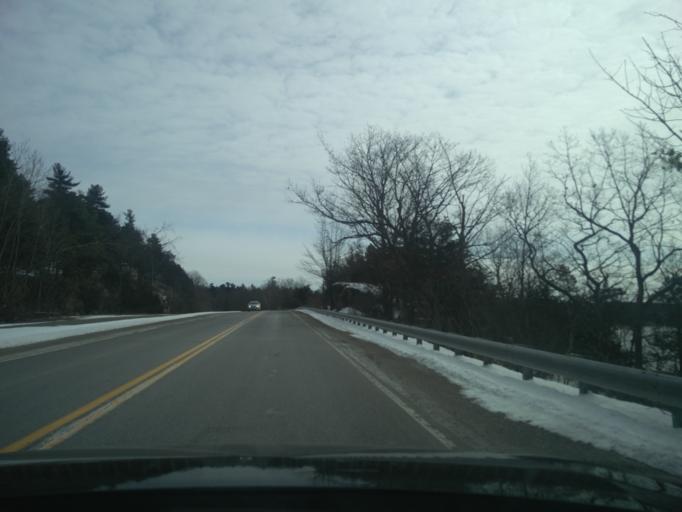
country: US
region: New York
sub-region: Jefferson County
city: Alexandria Bay
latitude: 44.3690
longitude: -75.9659
